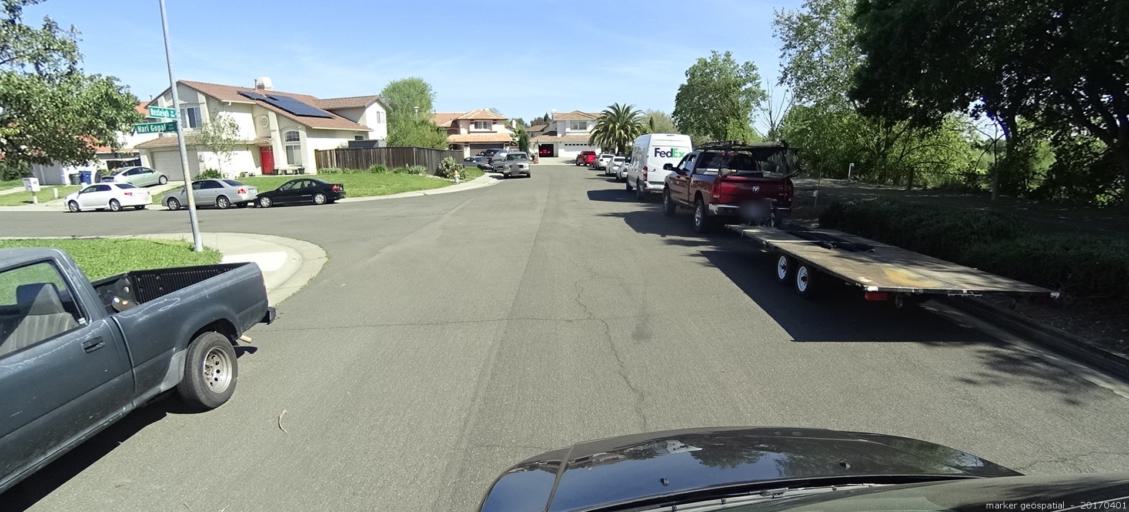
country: US
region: California
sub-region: Sacramento County
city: Laguna
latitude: 38.4442
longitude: -121.4394
